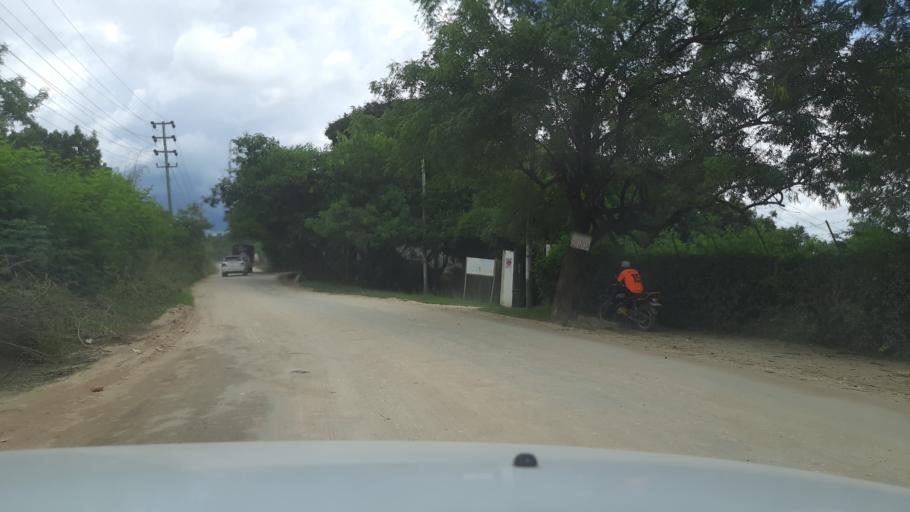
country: TZ
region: Dar es Salaam
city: Magomeni
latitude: -6.7571
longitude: 39.2093
